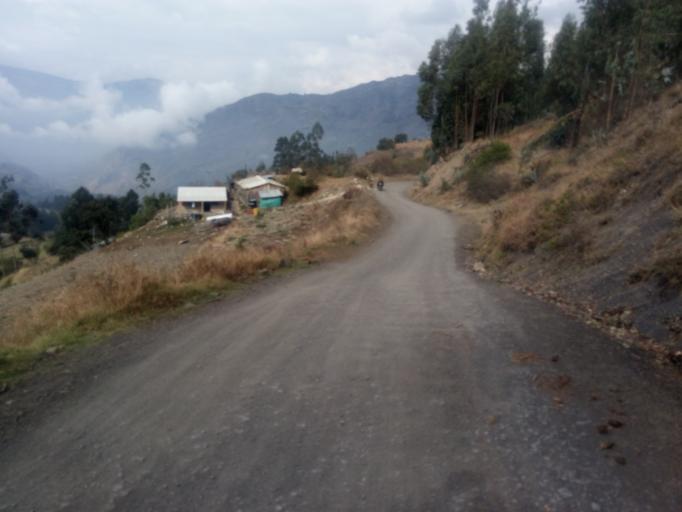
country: CO
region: Boyaca
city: Chita
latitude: 6.1924
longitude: -72.4774
